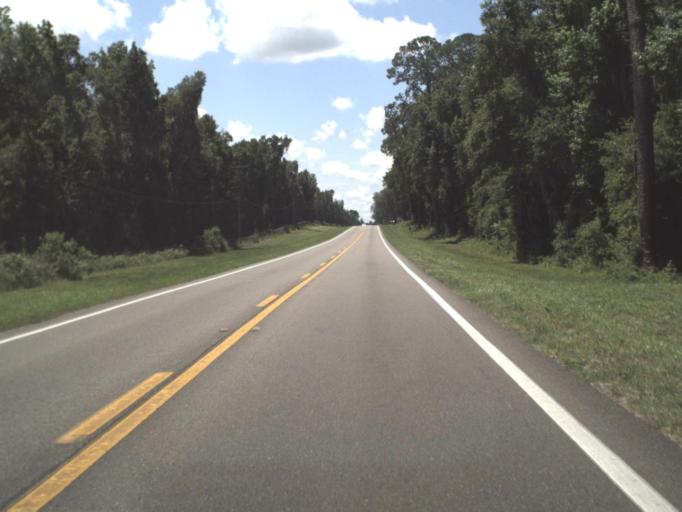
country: US
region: Florida
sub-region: Clay County
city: Keystone Heights
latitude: 29.7333
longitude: -82.0488
